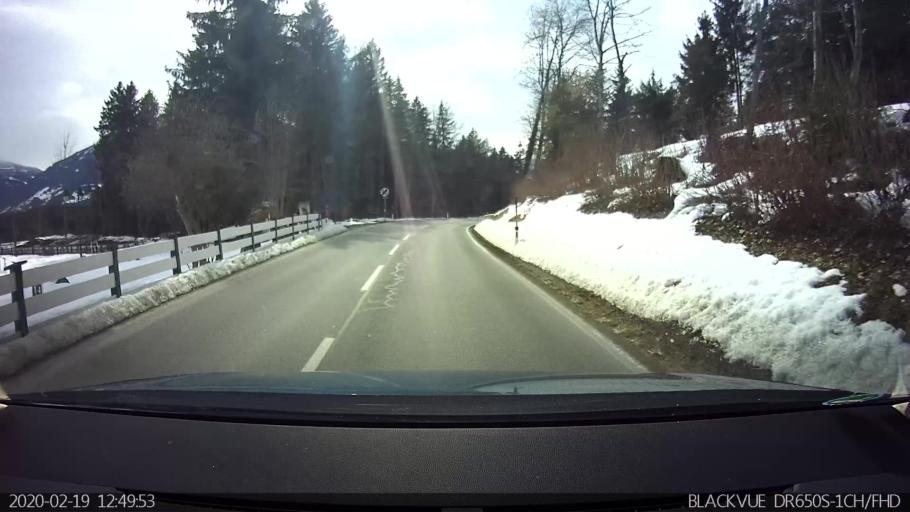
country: AT
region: Tyrol
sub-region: Politischer Bezirk Innsbruck Land
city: Gnadenwald
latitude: 47.3192
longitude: 11.5526
